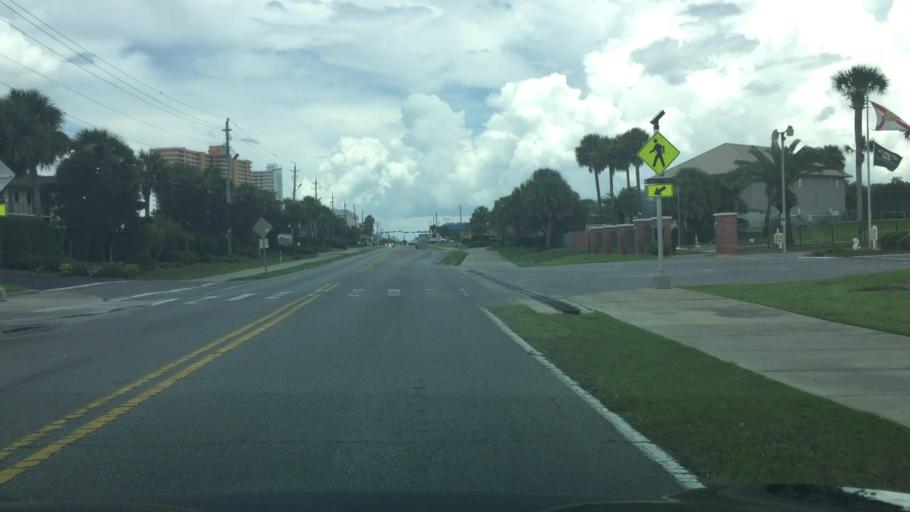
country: US
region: Florida
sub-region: Bay County
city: Lower Grand Lagoon
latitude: 30.1365
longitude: -85.7469
